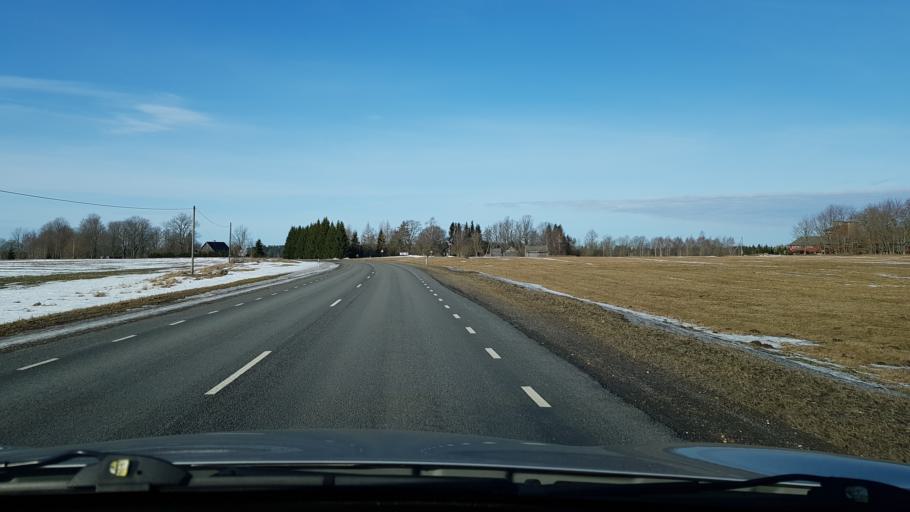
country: EE
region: Viljandimaa
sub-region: Suure-Jaani vald
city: Suure-Jaani
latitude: 58.5621
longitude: 25.4336
